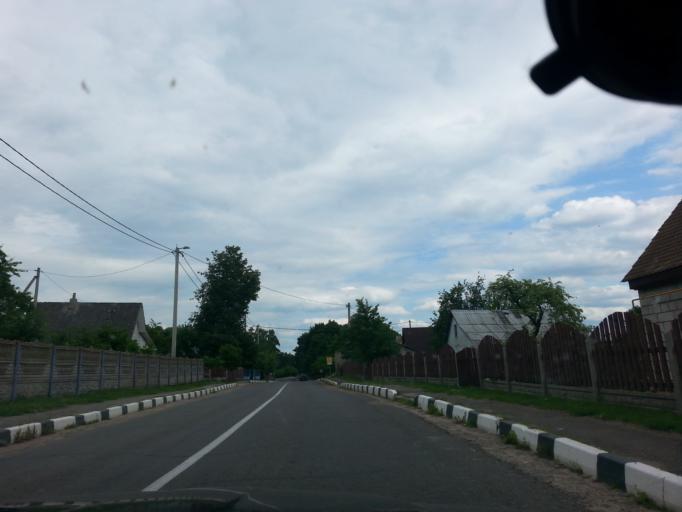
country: BY
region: Minsk
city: Narach
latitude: 54.8907
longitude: 26.7738
